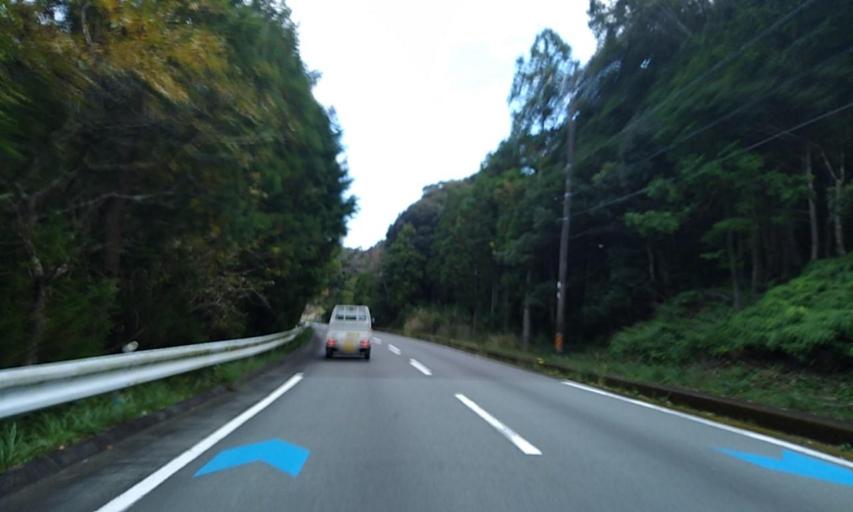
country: JP
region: Mie
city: Ise
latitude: 34.2996
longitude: 136.6089
